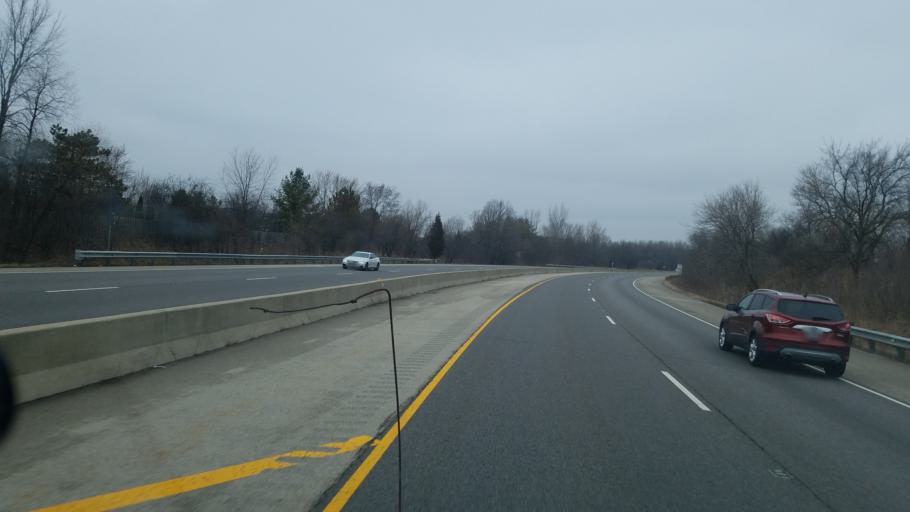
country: US
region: Illinois
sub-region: Lake County
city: Wadsworth
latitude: 42.4073
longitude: -87.9375
